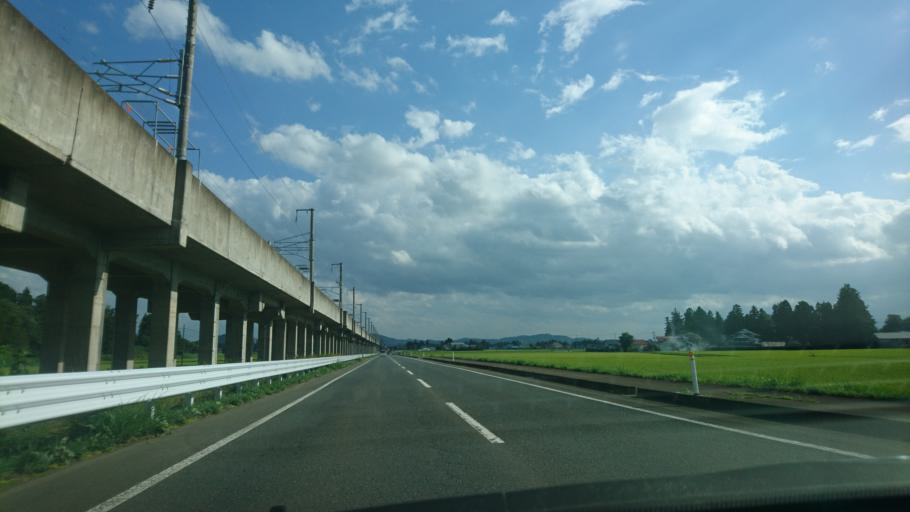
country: JP
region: Iwate
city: Hanamaki
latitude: 39.4494
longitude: 141.1762
